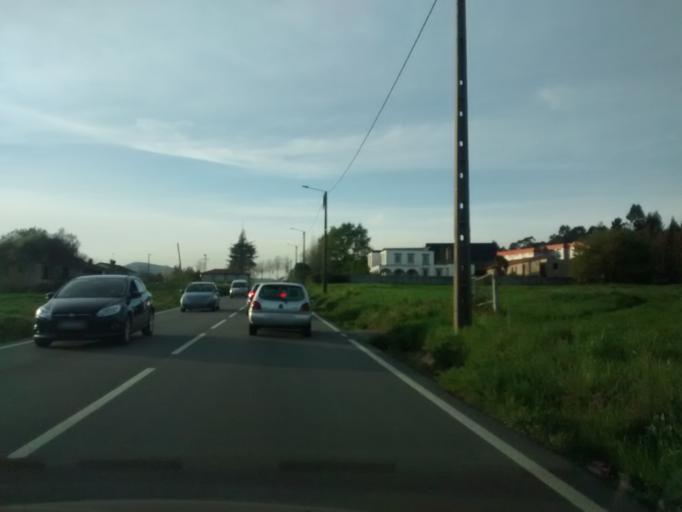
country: PT
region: Braga
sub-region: Guimaraes
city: Ponte
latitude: 41.4725
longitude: -8.3314
